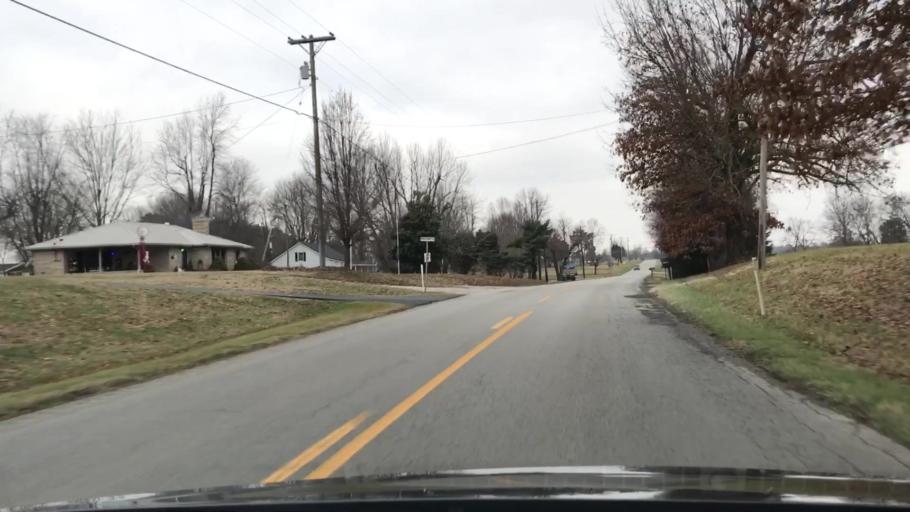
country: US
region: Kentucky
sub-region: Muhlenberg County
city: Morehead
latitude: 37.3903
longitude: -87.2543
